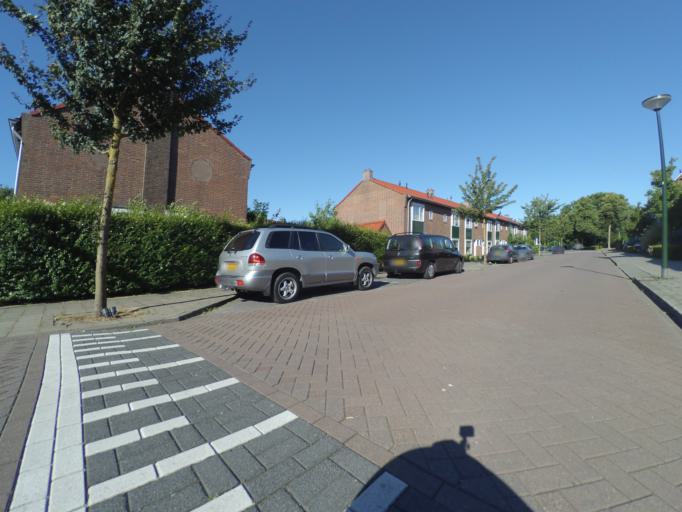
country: NL
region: North Holland
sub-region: Gemeente Weesp
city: Weesp
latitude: 52.3033
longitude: 5.0393
